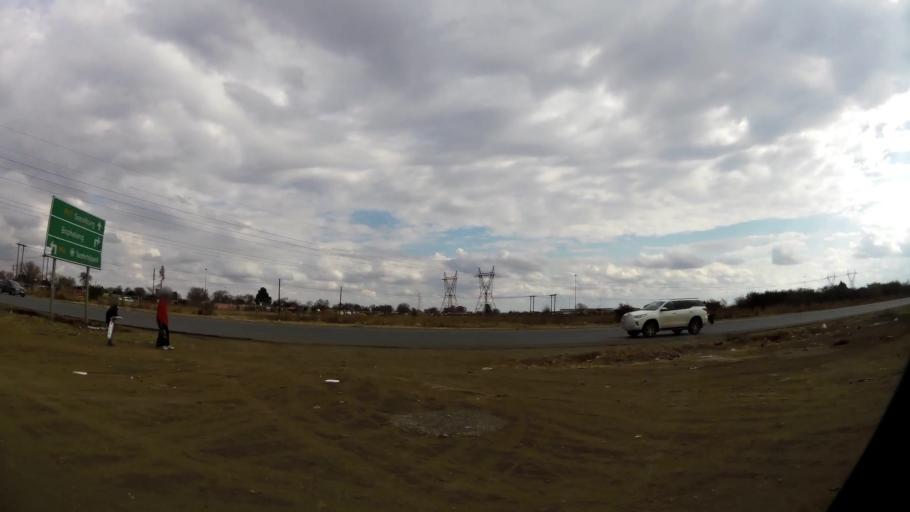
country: ZA
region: Gauteng
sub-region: Sedibeng District Municipality
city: Vanderbijlpark
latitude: -26.6888
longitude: 27.8023
